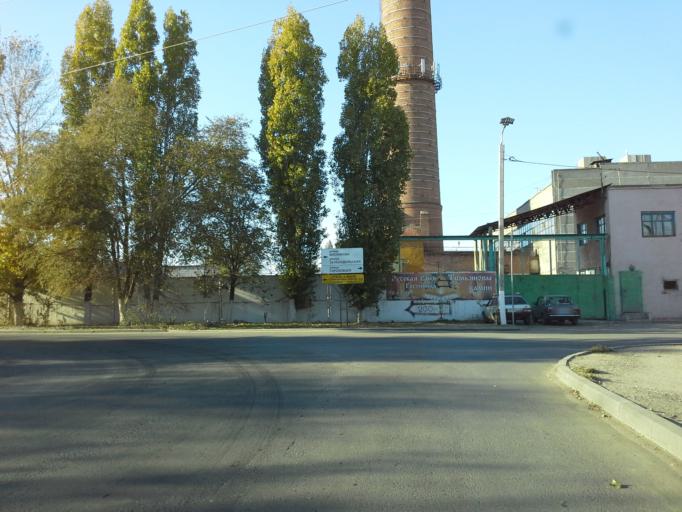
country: RU
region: Volgograd
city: Vodstroy
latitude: 48.8249
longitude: 44.6280
